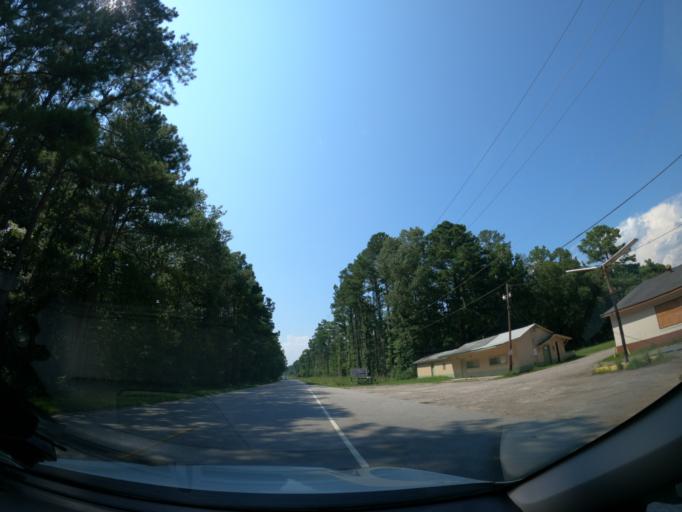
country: US
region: South Carolina
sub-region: Richland County
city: Hopkins
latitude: 33.9030
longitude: -80.9270
